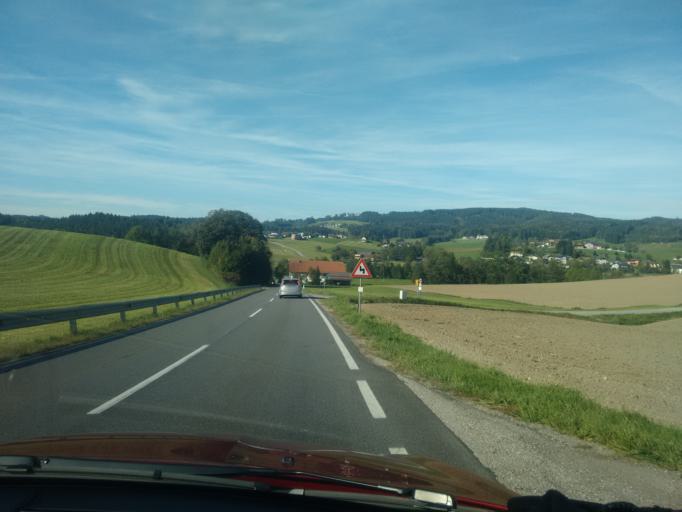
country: AT
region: Upper Austria
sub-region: Politischer Bezirk Vocklabruck
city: Zell am Pettenfirst
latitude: 48.0761
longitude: 13.5736
